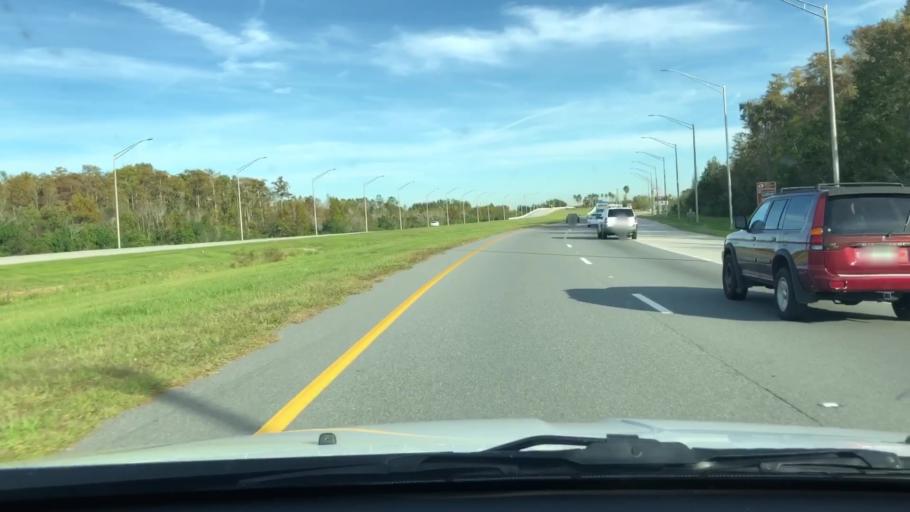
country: US
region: Florida
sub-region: Orange County
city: Meadow Woods
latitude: 28.3901
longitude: -81.3099
